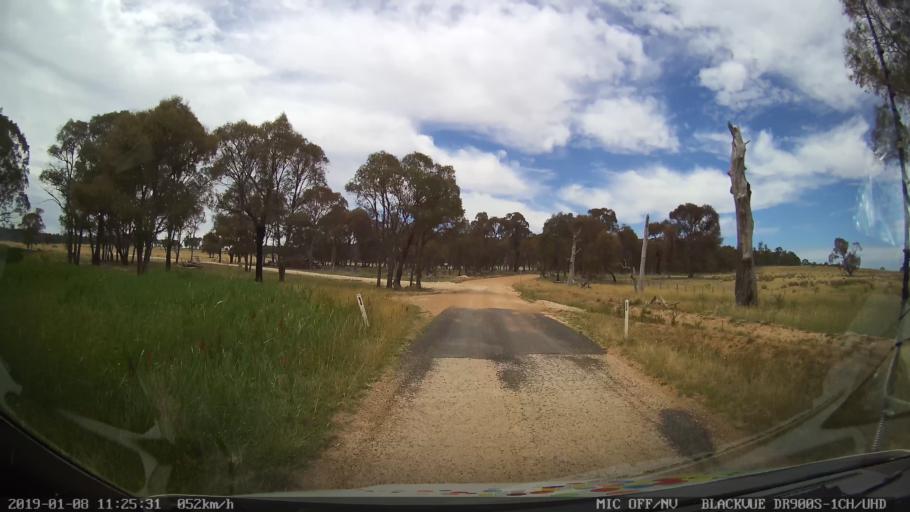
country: AU
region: New South Wales
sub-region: Guyra
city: Guyra
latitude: -30.2741
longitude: 151.5612
